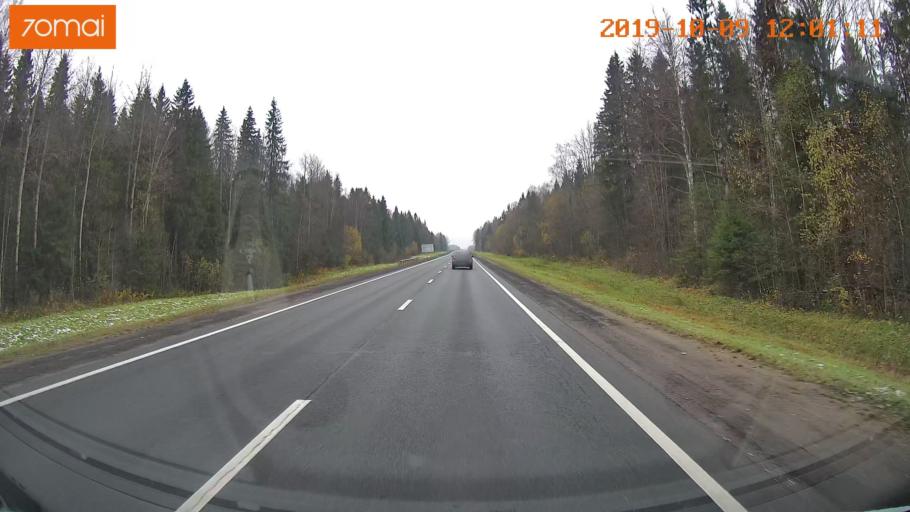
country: RU
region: Vologda
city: Gryazovets
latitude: 58.6909
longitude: 40.3022
